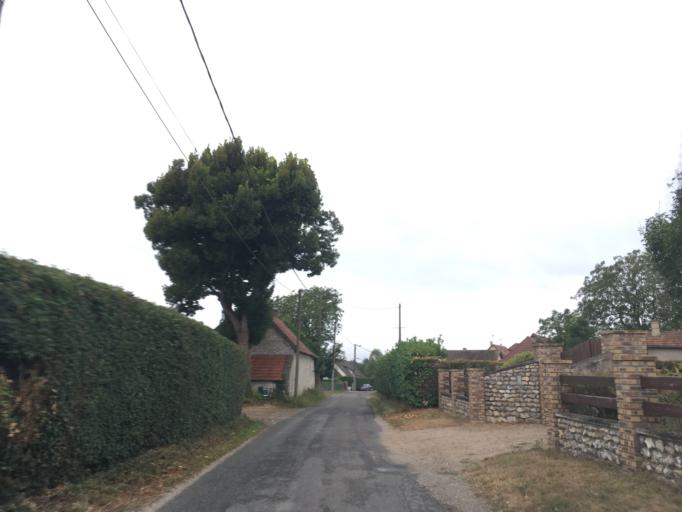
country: FR
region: Ile-de-France
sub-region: Departement des Yvelines
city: Limetz-Villez
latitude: 49.1013
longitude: 1.5388
